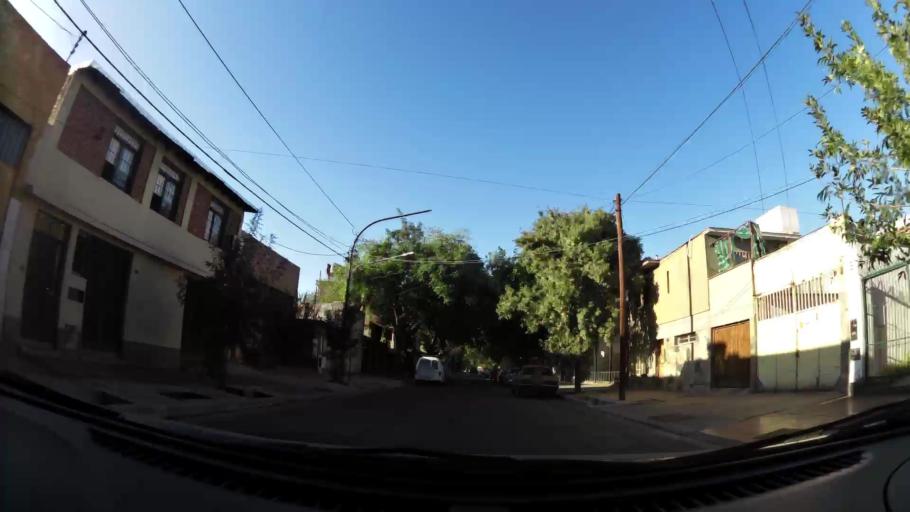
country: AR
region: Mendoza
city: Mendoza
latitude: -32.8771
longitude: -68.8295
